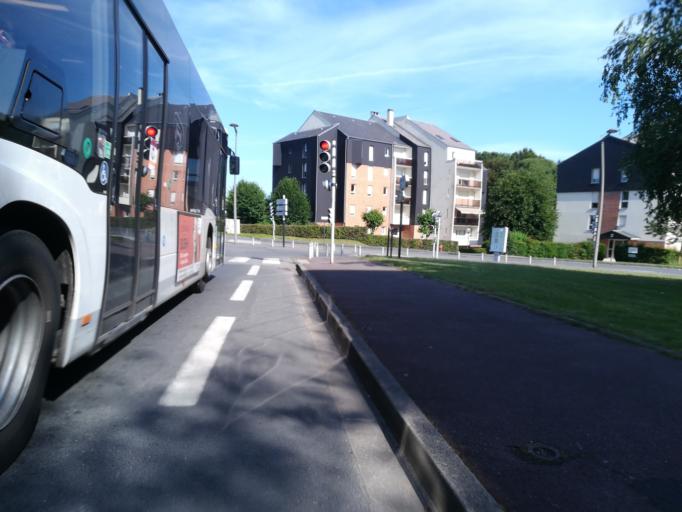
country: FR
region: Haute-Normandie
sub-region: Departement de la Seine-Maritime
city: Mont-Saint-Aignan
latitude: 49.4612
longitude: 1.0737
